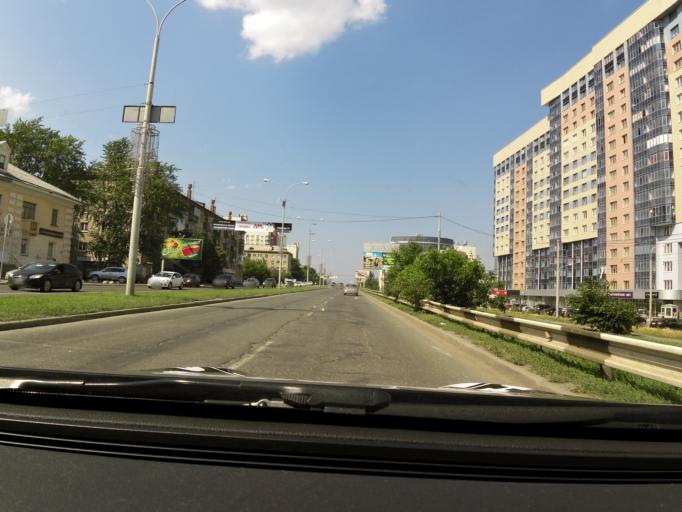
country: RU
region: Sverdlovsk
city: Yekaterinburg
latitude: 56.8256
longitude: 60.5858
